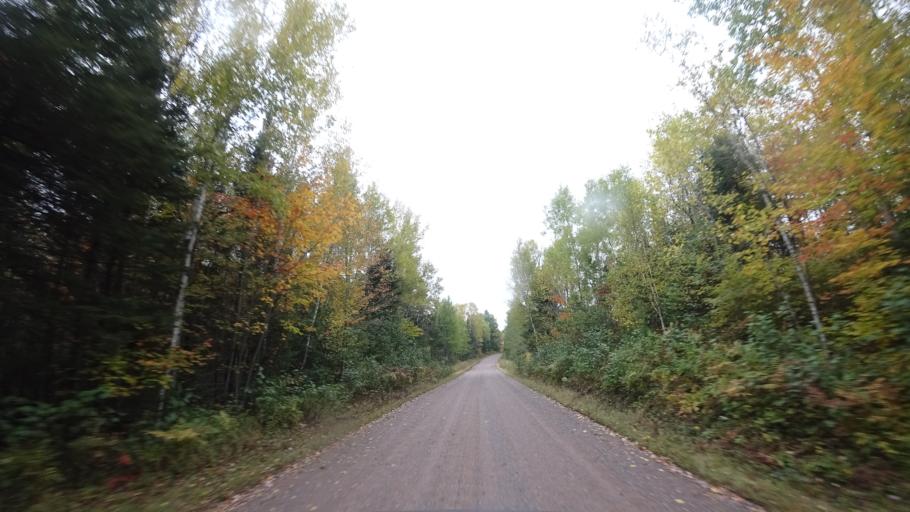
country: US
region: Wisconsin
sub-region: Sawyer County
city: Little Round Lake
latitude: 46.0691
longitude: -90.9944
